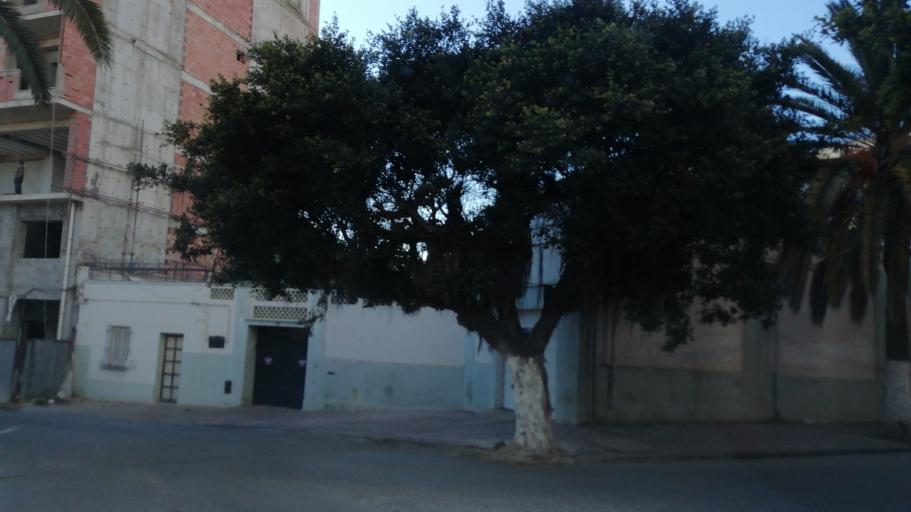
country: DZ
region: Oran
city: Oran
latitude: 35.7105
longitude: -0.6166
